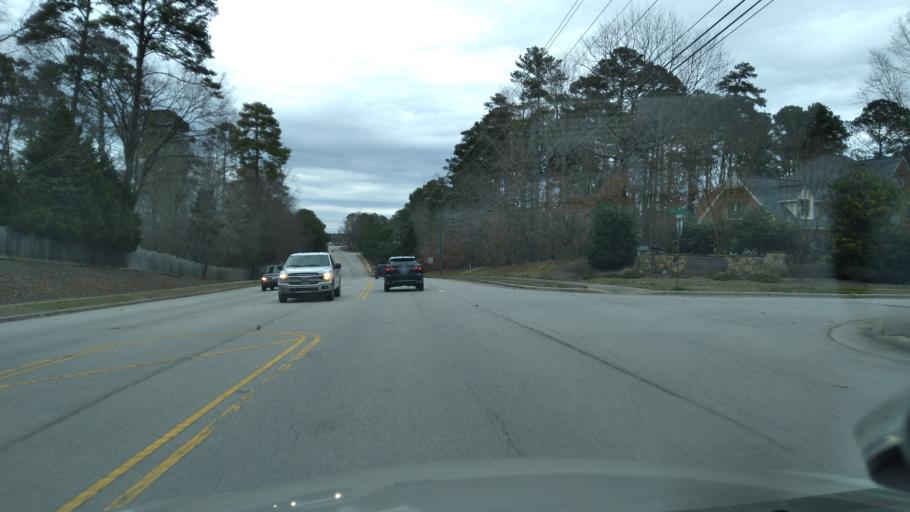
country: US
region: North Carolina
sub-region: Wake County
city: Apex
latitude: 35.7391
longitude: -78.8264
